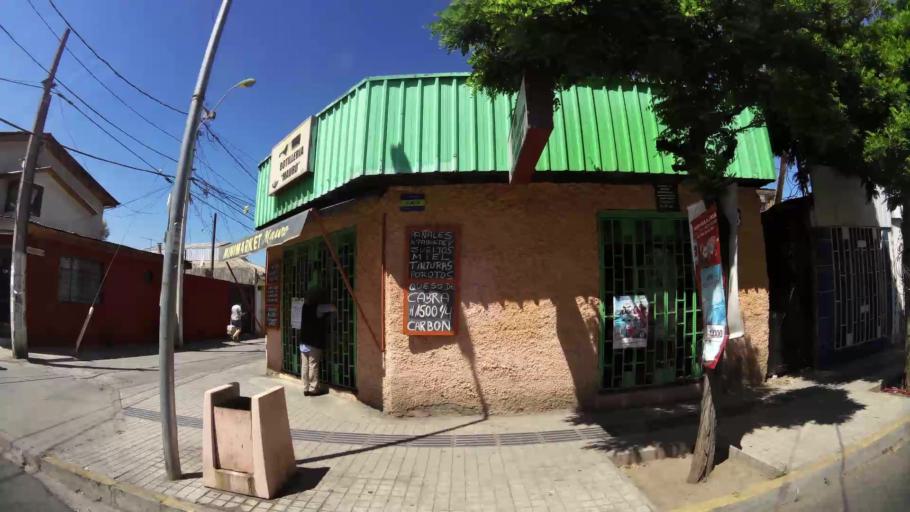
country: CL
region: Santiago Metropolitan
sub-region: Provincia de Maipo
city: San Bernardo
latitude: -33.5648
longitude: -70.6799
